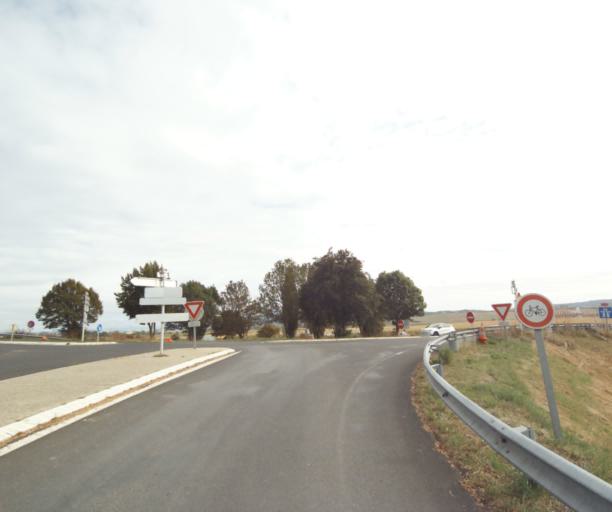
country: FR
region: Auvergne
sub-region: Departement du Puy-de-Dome
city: Perignat-les-Sarlieve
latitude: 45.7343
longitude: 3.1516
